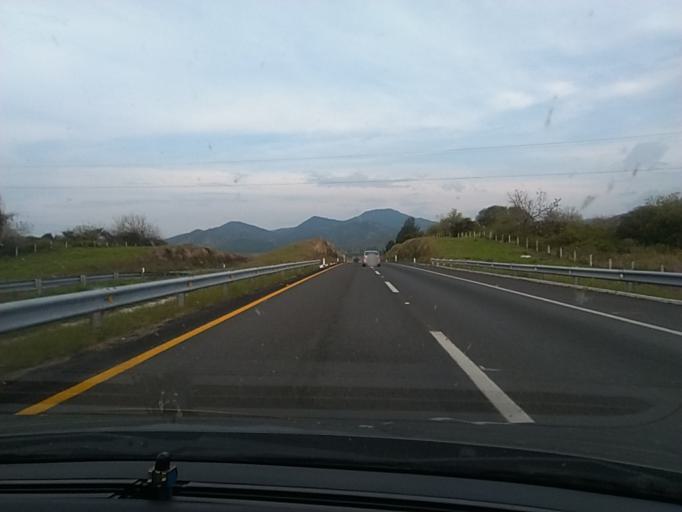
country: MX
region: Michoacan
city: Zinapecuaro
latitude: 19.9021
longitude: -100.8072
